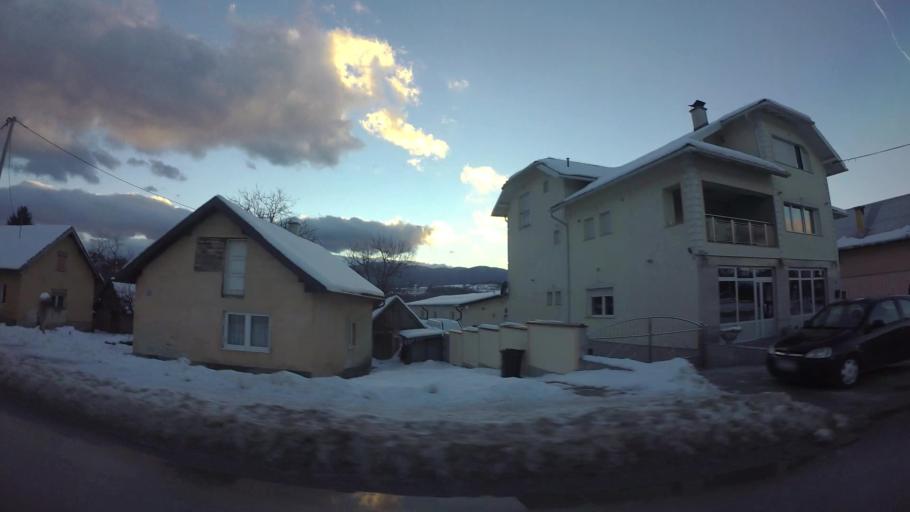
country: BA
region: Federation of Bosnia and Herzegovina
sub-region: Kanton Sarajevo
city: Sarajevo
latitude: 43.8084
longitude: 18.3759
